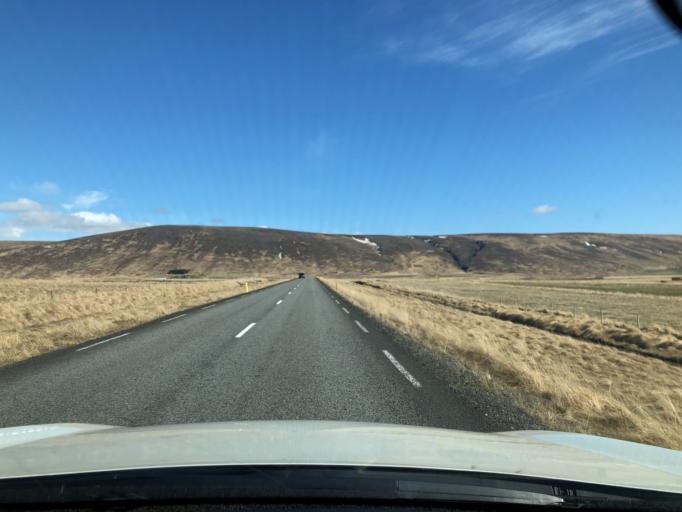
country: IS
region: South
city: Hveragerdi
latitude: 64.6890
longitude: -21.2406
